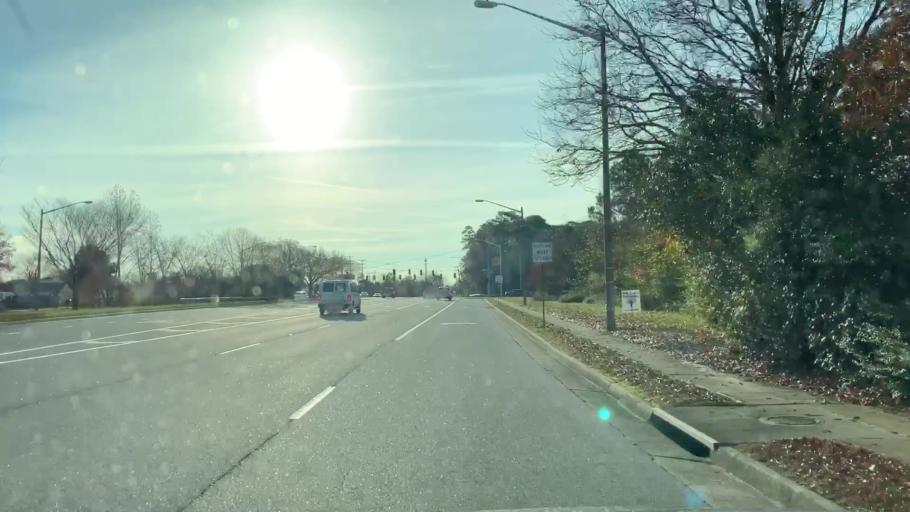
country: US
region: Virginia
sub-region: City of Chesapeake
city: Chesapeake
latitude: 36.7866
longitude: -76.1618
